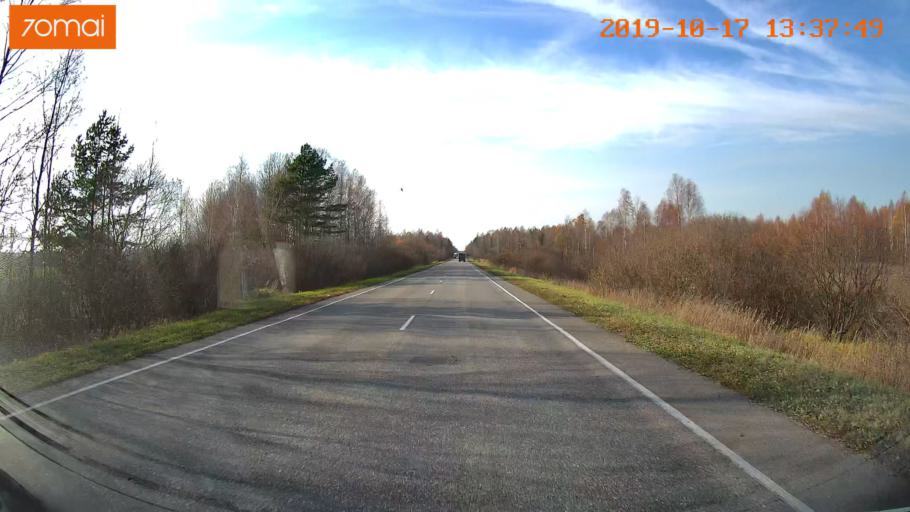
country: RU
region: Rjazan
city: Tuma
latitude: 55.1425
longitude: 40.6292
